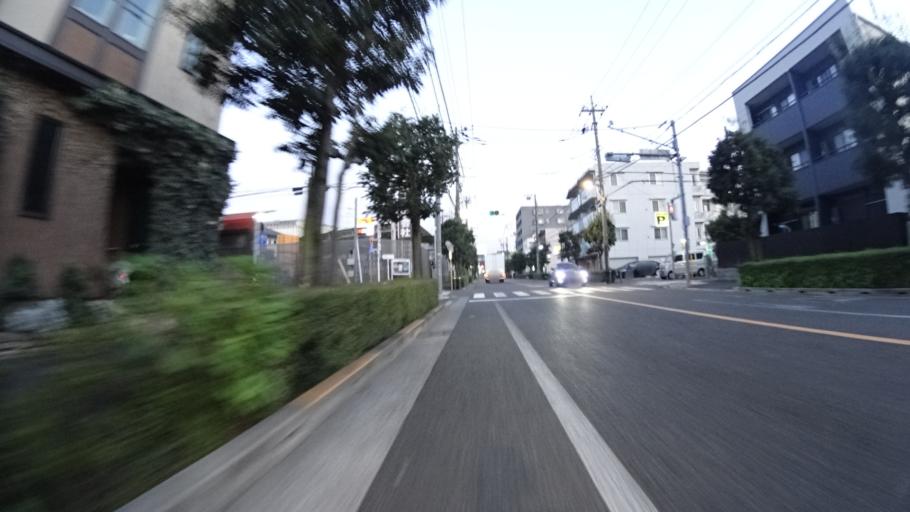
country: JP
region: Tokyo
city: Chofugaoka
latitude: 35.6560
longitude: 139.5272
